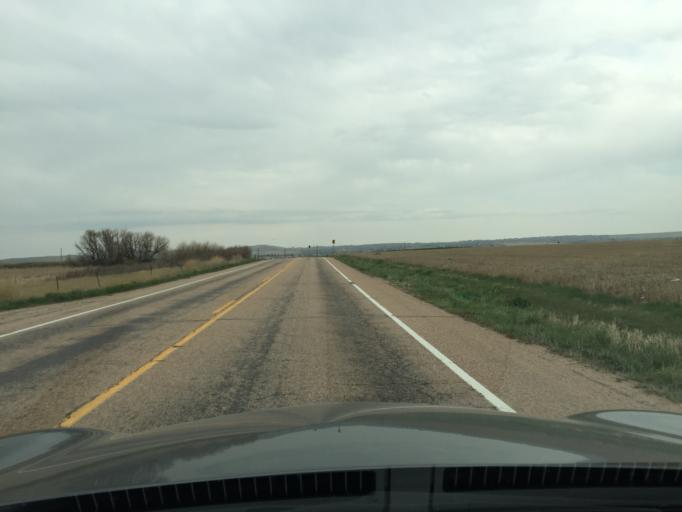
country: US
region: Colorado
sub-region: Boulder County
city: Lafayette
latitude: 40.0147
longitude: -105.0805
